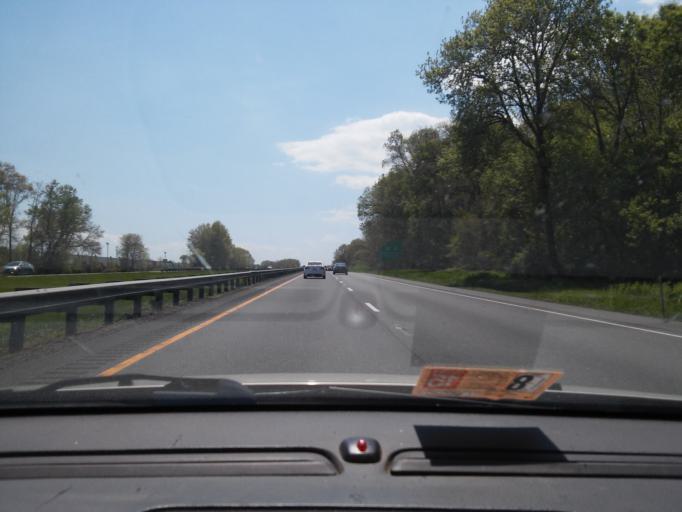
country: US
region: Maryland
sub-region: Washington County
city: Williamsport
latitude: 39.6000
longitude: -77.8062
